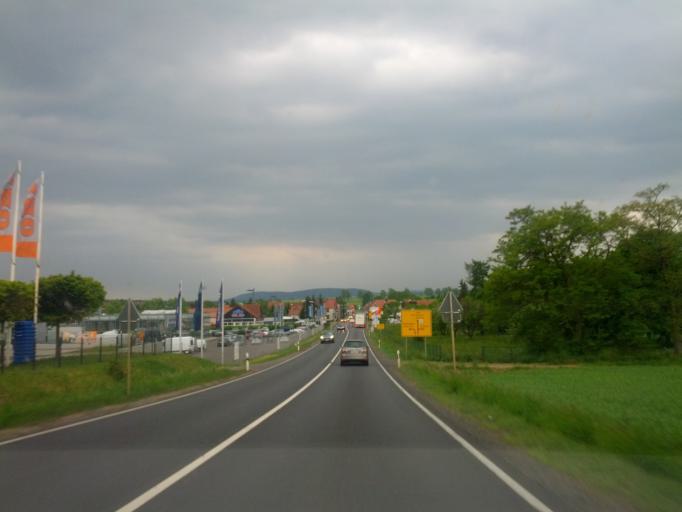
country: DE
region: Thuringia
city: Schwabhausen
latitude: 50.8934
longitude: 10.7278
